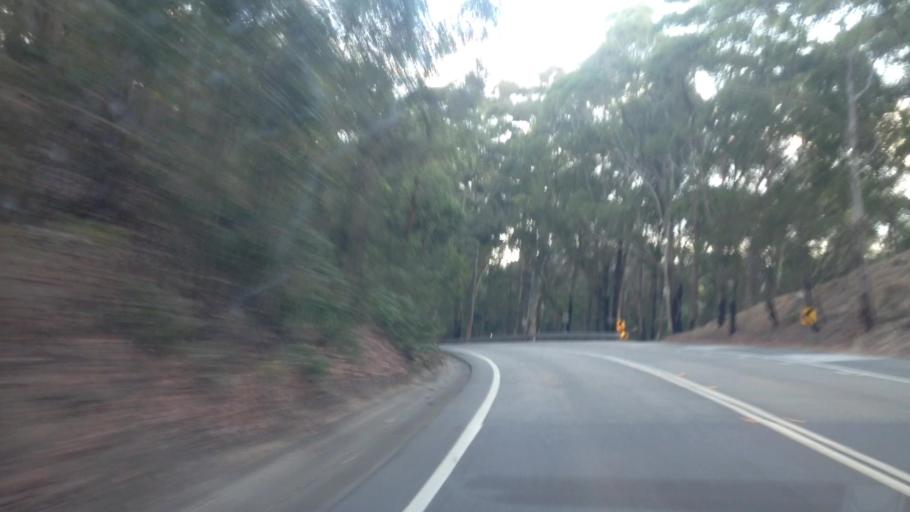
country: AU
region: New South Wales
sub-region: Lake Macquarie Shire
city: Cooranbong
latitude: -32.9681
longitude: 151.4801
